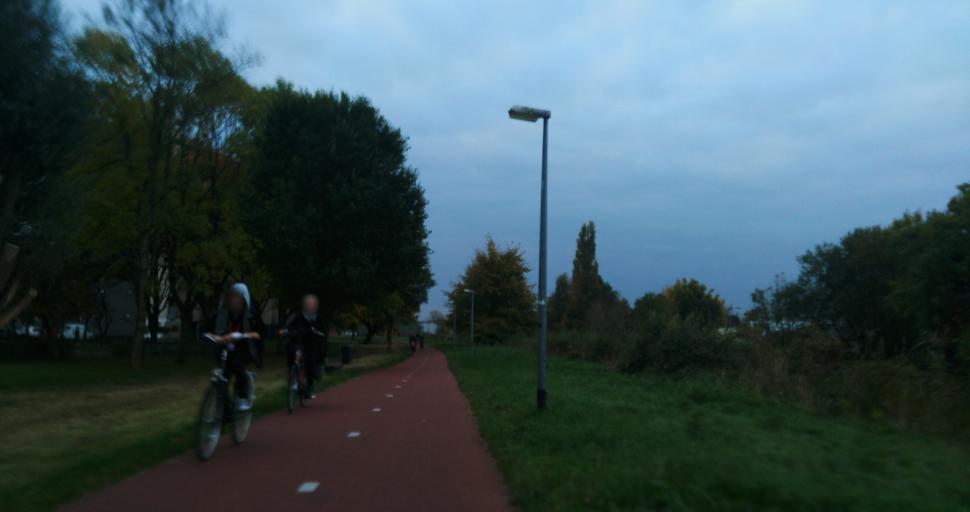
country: NL
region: Groningen
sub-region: Gemeente Groningen
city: Groningen
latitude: 53.2261
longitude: 6.5367
